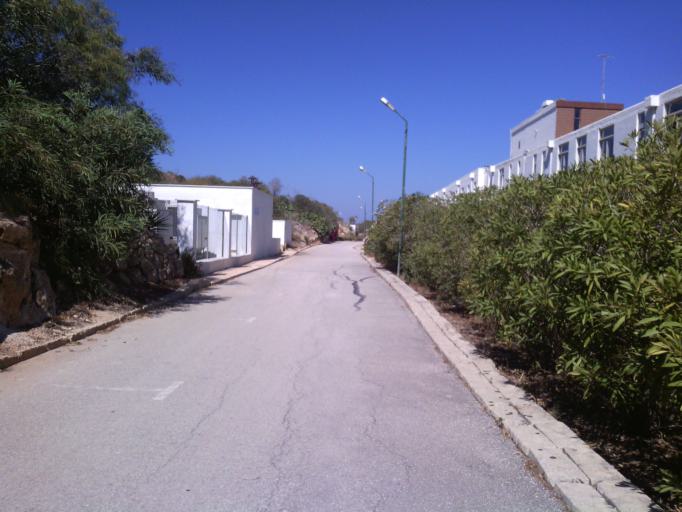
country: MT
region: Il-Mellieha
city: Mellieha
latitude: 35.9761
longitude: 14.3524
